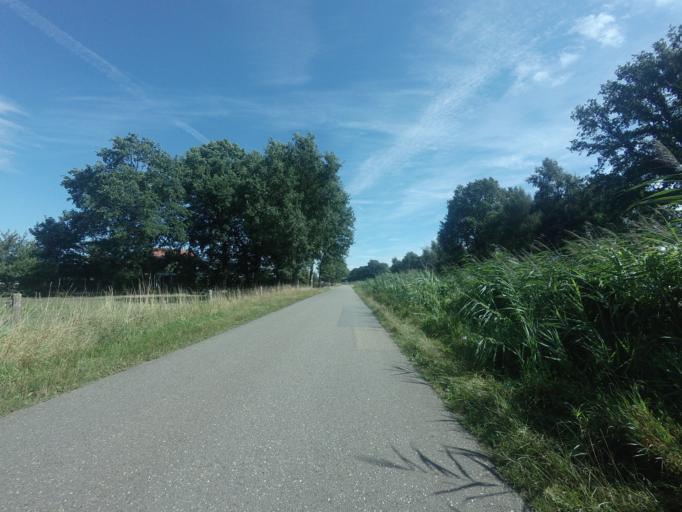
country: NL
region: Overijssel
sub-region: Gemeente Raalte
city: Raalte
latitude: 52.4077
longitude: 6.3067
